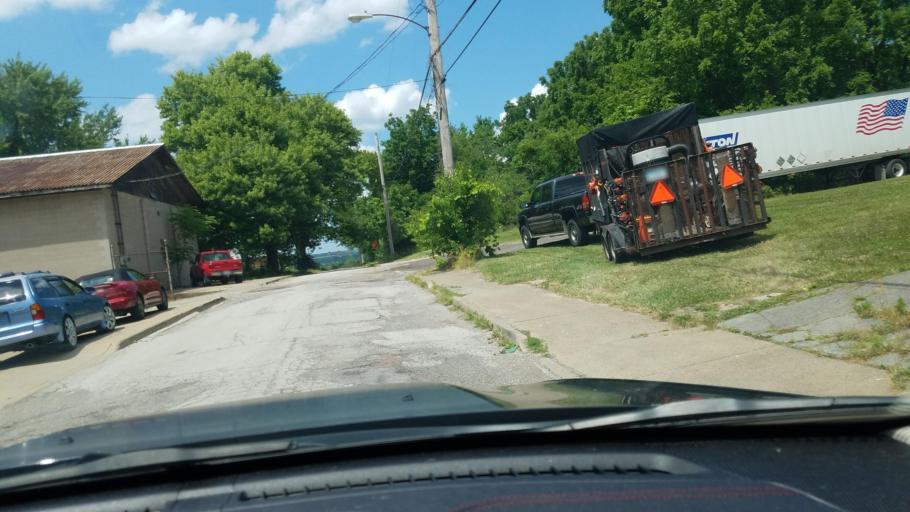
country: US
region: Ohio
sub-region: Mahoning County
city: Youngstown
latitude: 41.0946
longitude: -80.6318
